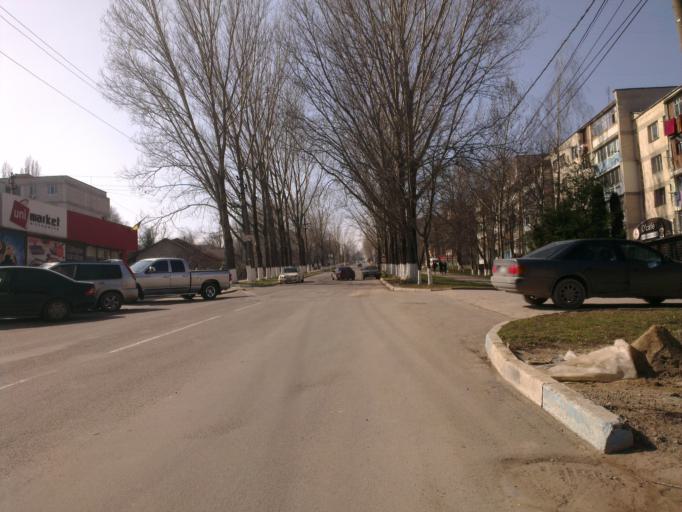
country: MD
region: Chisinau
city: Cricova
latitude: 47.1396
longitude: 28.8648
